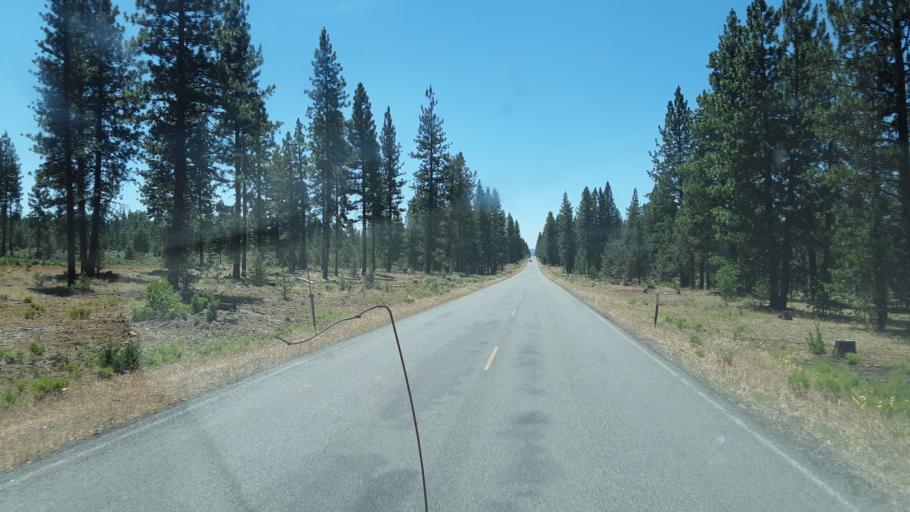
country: US
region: California
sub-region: Siskiyou County
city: Tulelake
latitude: 41.4147
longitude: -121.1765
